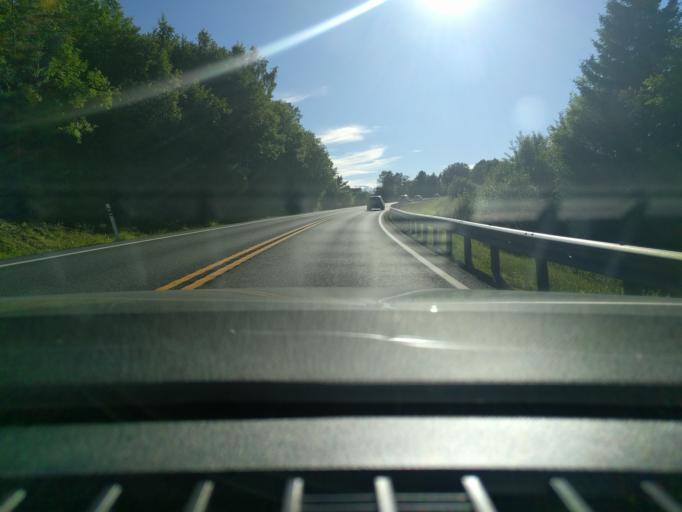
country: NO
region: Buskerud
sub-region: Royken
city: Royken
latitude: 59.7330
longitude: 10.3563
